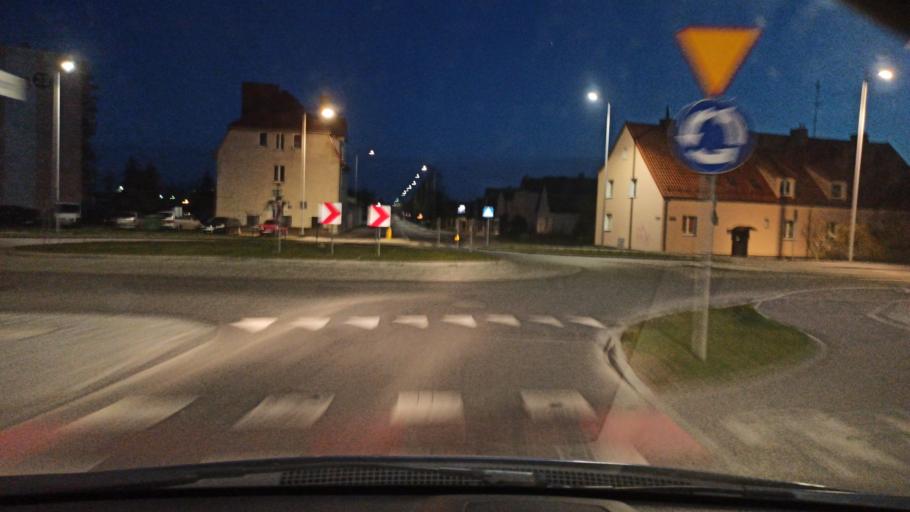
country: PL
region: Warmian-Masurian Voivodeship
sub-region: Powiat elblaski
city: Elblag
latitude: 54.1498
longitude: 19.4125
